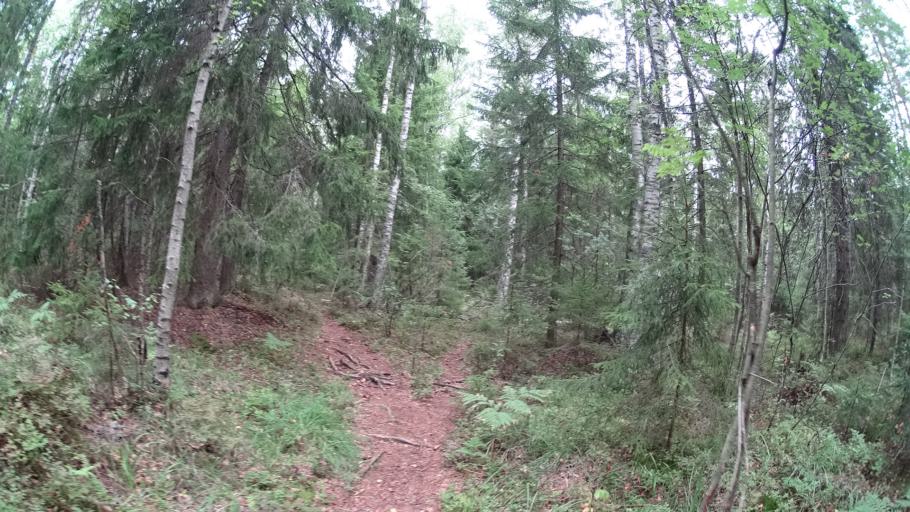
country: FI
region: Uusimaa
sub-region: Helsinki
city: Espoo
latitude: 60.3084
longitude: 24.5800
